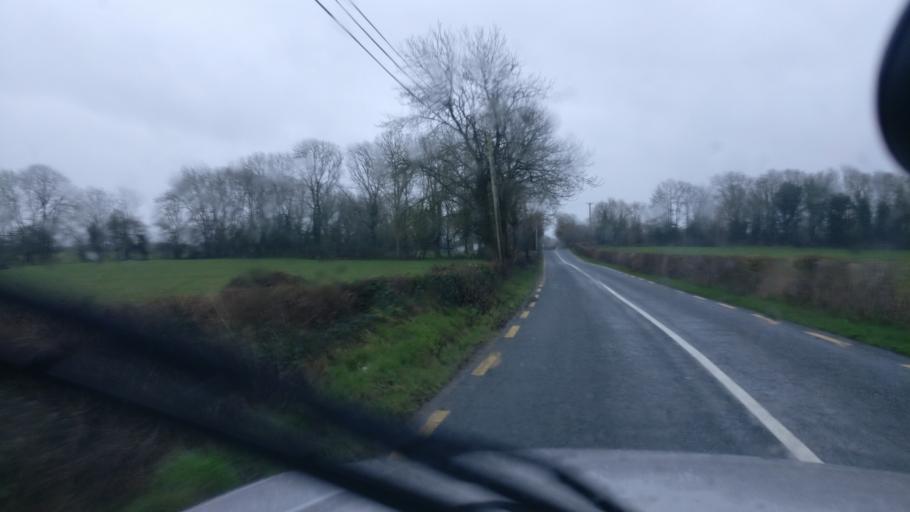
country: IE
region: Connaught
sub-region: County Galway
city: Ballinasloe
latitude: 53.2248
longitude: -8.1945
